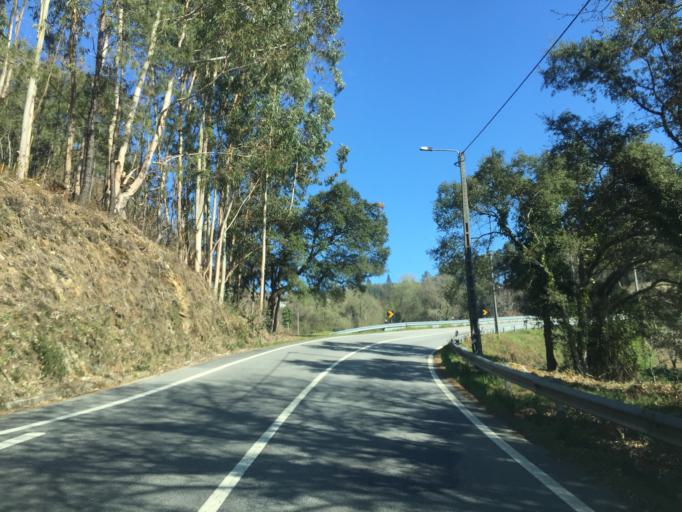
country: PT
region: Aveiro
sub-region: Vale de Cambra
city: Macieira de Cambra
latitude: 40.8900
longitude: -8.3589
